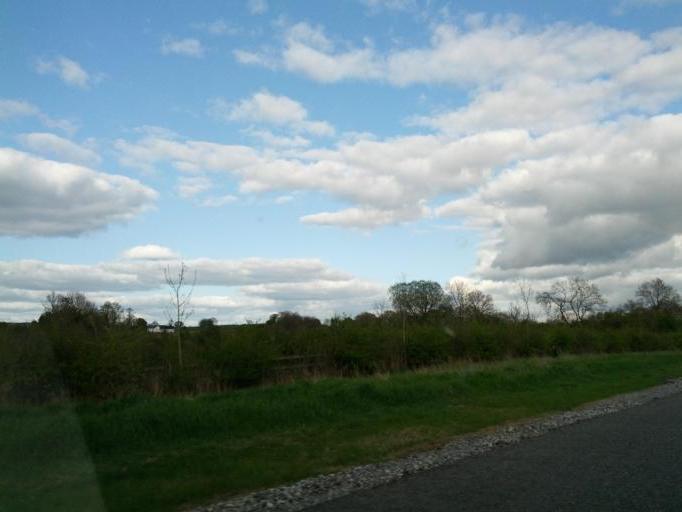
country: IE
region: Leinster
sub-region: Uibh Fhaili
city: Clara
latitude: 53.3822
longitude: -7.5734
